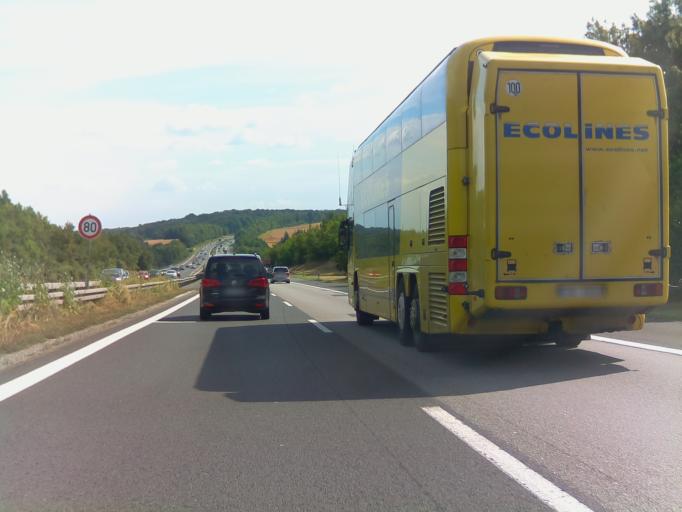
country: DE
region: Bavaria
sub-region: Regierungsbezirk Unterfranken
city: Arnstein
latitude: 49.9673
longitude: 10.0330
